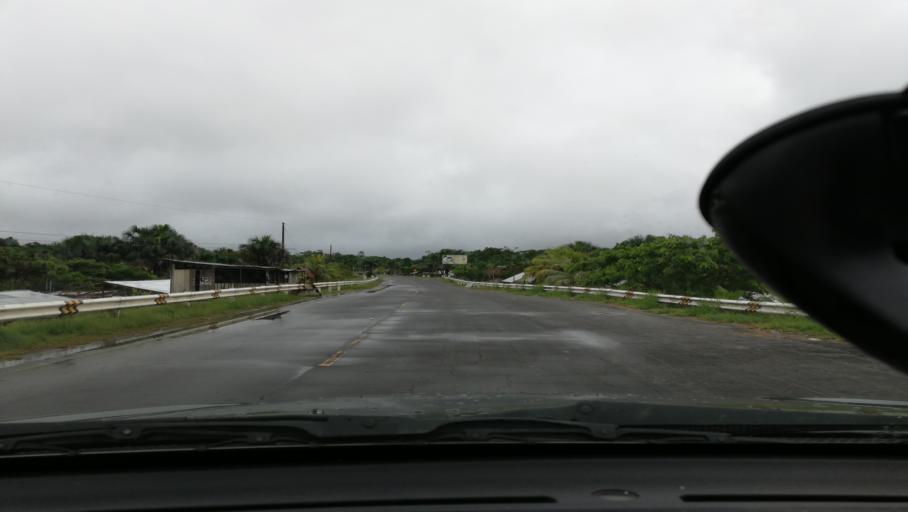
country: PE
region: Loreto
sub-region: Provincia de Loreto
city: Nauta
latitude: -4.2227
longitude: -73.4824
